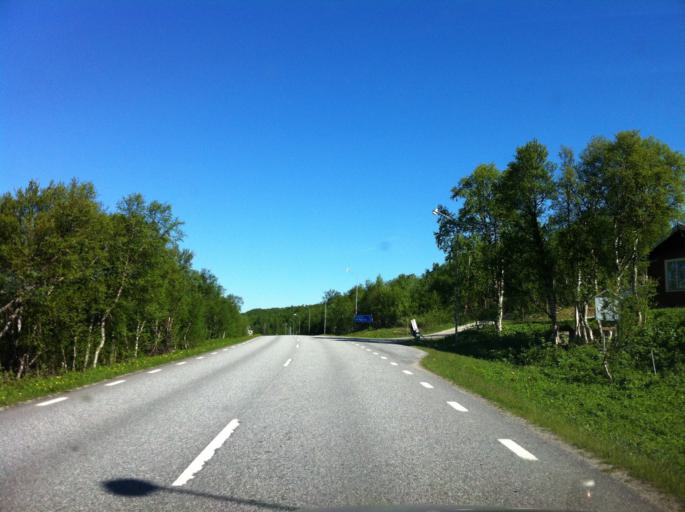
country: NO
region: Sor-Trondelag
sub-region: Tydal
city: Aas
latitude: 62.5673
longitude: 12.2476
